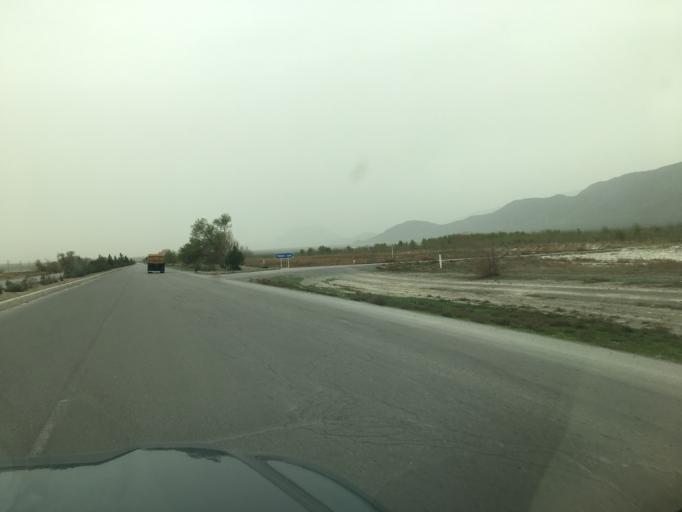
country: TM
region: Ahal
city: Arcabil
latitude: 38.1934
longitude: 57.8381
